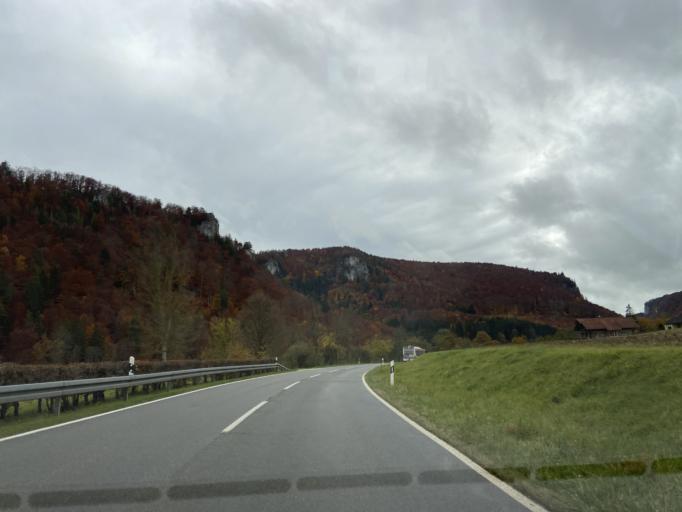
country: DE
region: Baden-Wuerttemberg
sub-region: Tuebingen Region
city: Leibertingen
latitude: 48.0746
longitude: 9.0225
